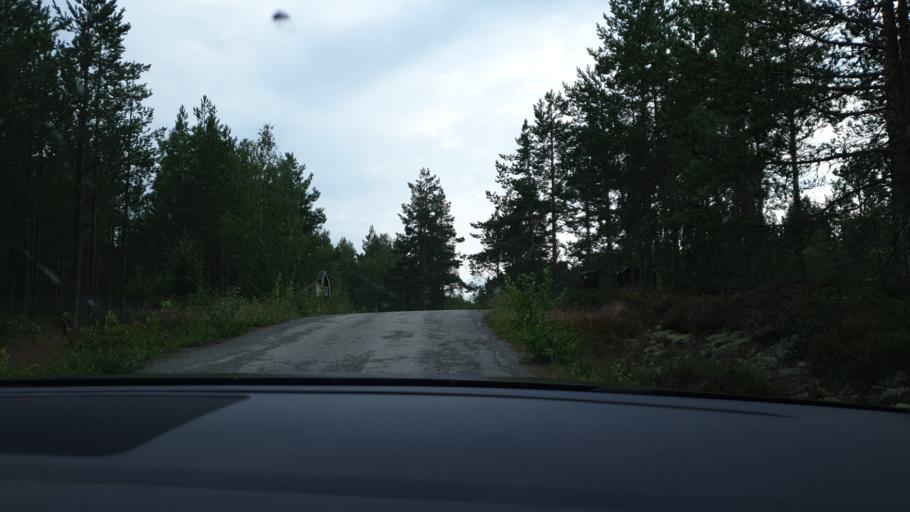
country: SE
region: Gaevleborg
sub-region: Hudiksvalls Kommun
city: Iggesund
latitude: 61.5314
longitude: 17.0119
